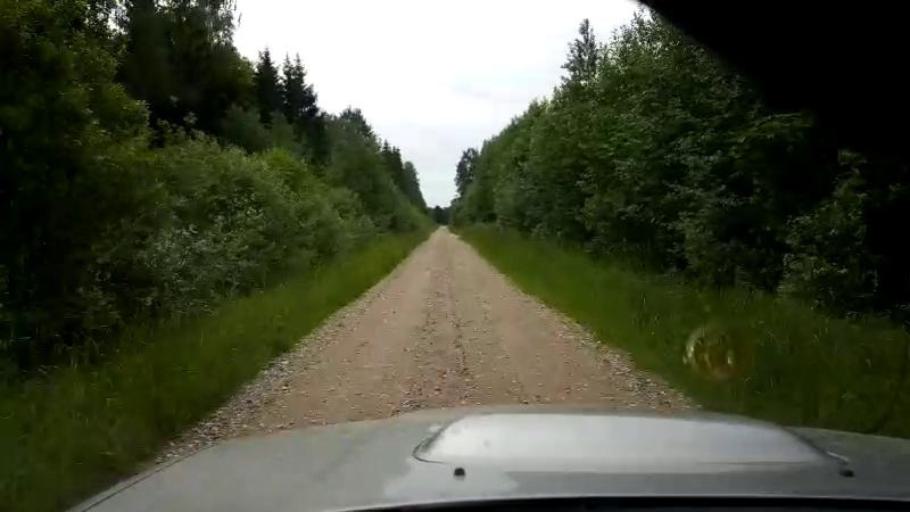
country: EE
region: Paernumaa
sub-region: Tootsi vald
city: Tootsi
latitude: 58.5537
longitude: 24.7470
